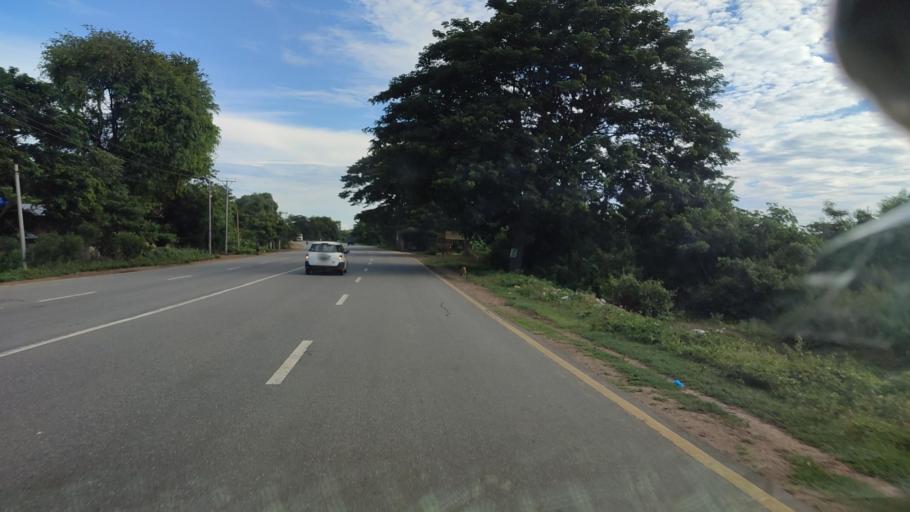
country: MM
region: Mandalay
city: Yamethin
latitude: 20.2066
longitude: 96.1807
